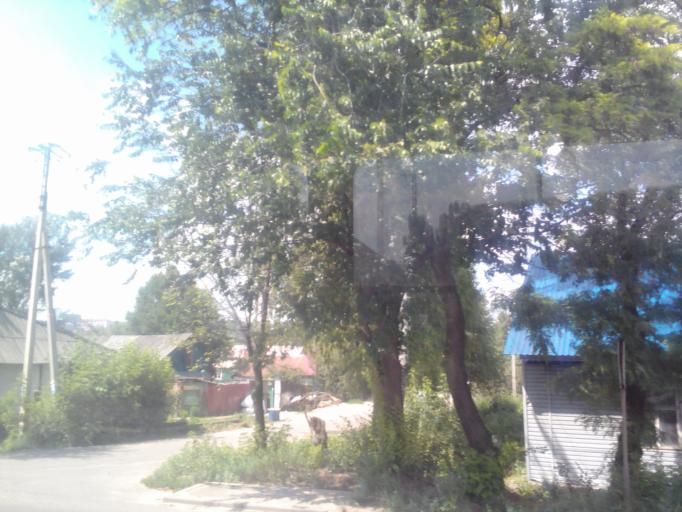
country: RU
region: Kursk
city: Kursk
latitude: 51.7114
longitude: 36.1848
